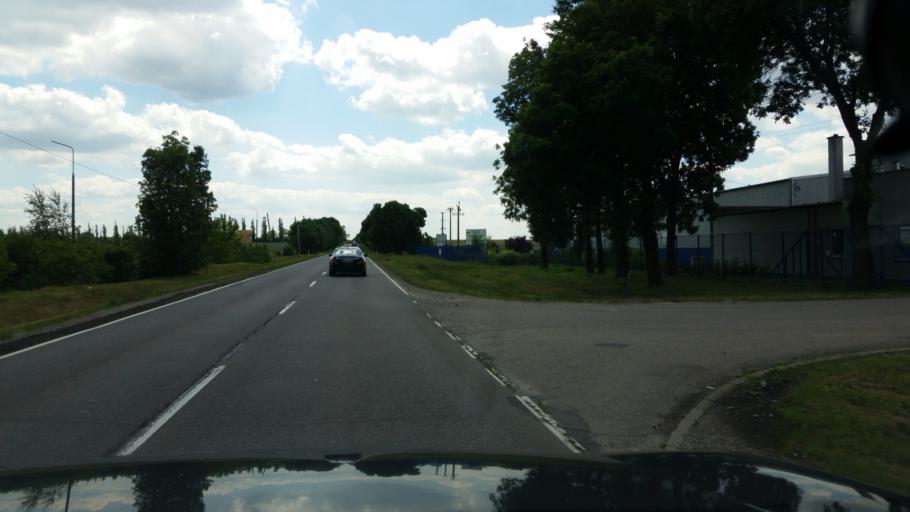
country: PL
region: Masovian Voivodeship
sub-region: Powiat ostrowski
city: Ostrow Mazowiecka
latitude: 52.8491
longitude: 21.8683
